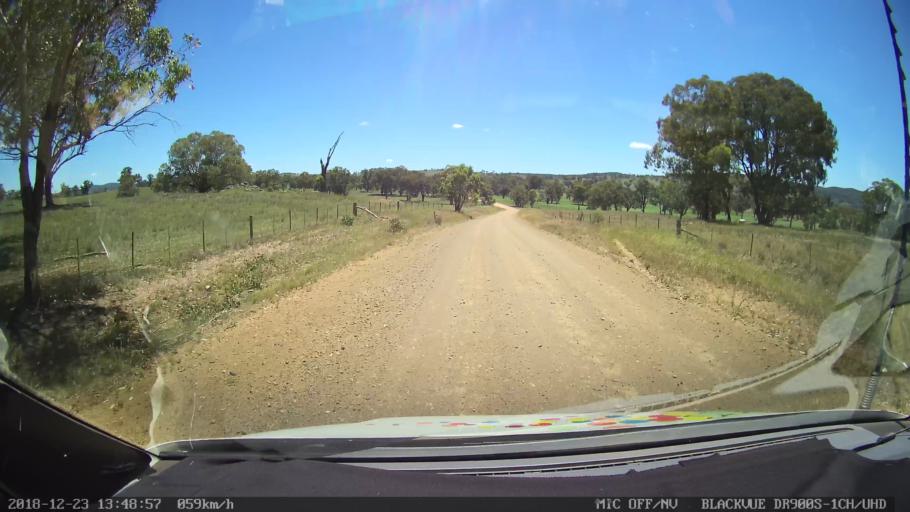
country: AU
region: New South Wales
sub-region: Tamworth Municipality
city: Manilla
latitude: -30.5198
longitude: 151.1124
